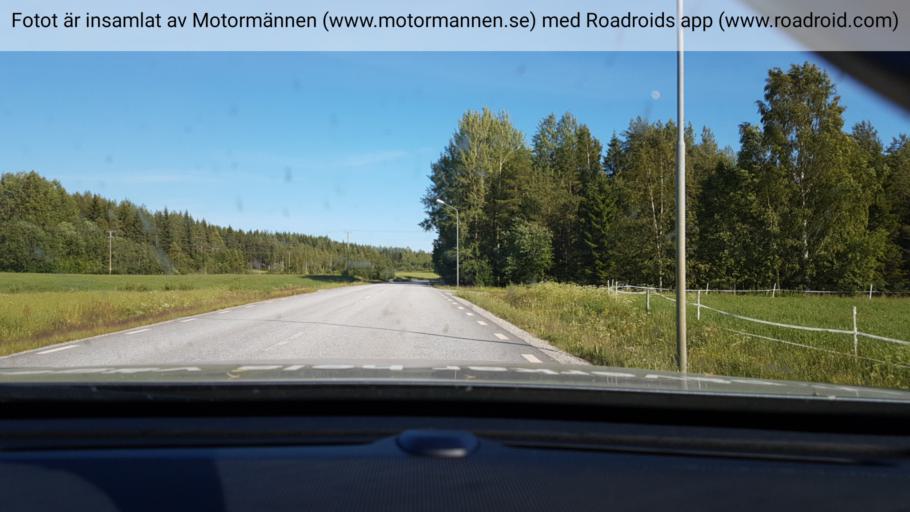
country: SE
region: Vaesterbotten
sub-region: Vindelns Kommun
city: Vindeln
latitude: 64.1242
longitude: 19.5562
